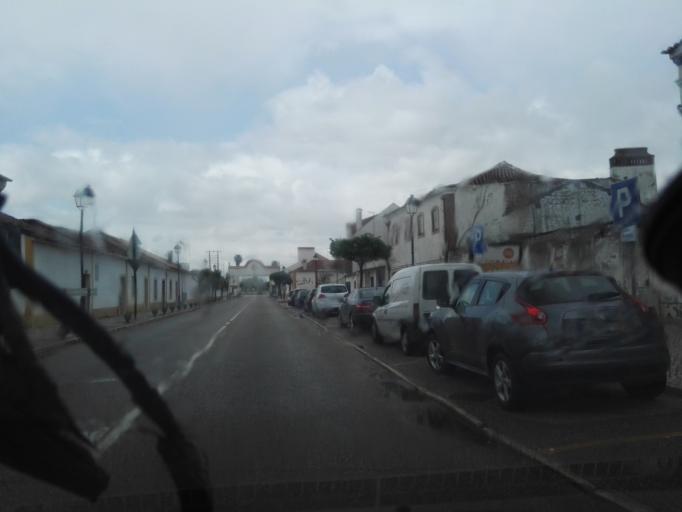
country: PT
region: Santarem
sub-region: Golega
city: Golega
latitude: 39.4073
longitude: -8.4857
